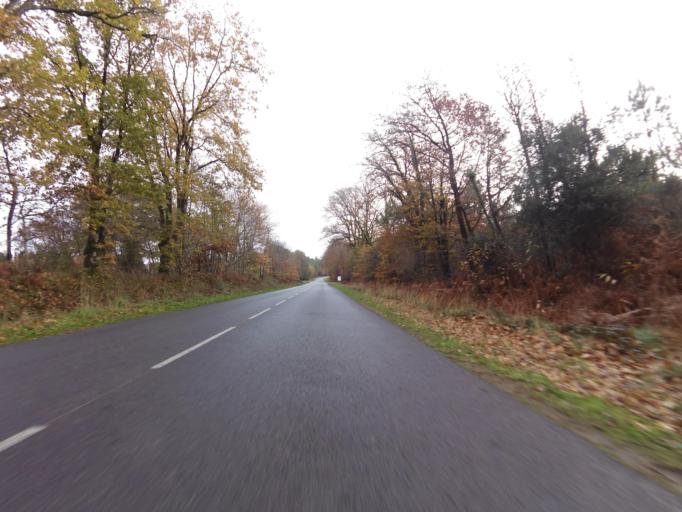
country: FR
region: Brittany
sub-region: Departement du Morbihan
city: Saint-Martin-sur-Oust
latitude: 47.7252
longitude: -2.2730
